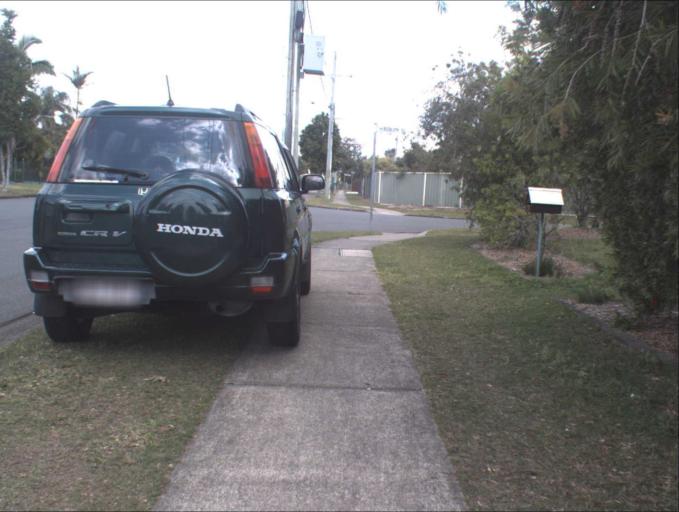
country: AU
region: Queensland
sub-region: Logan
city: Logan Reserve
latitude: -27.6829
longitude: 153.0854
